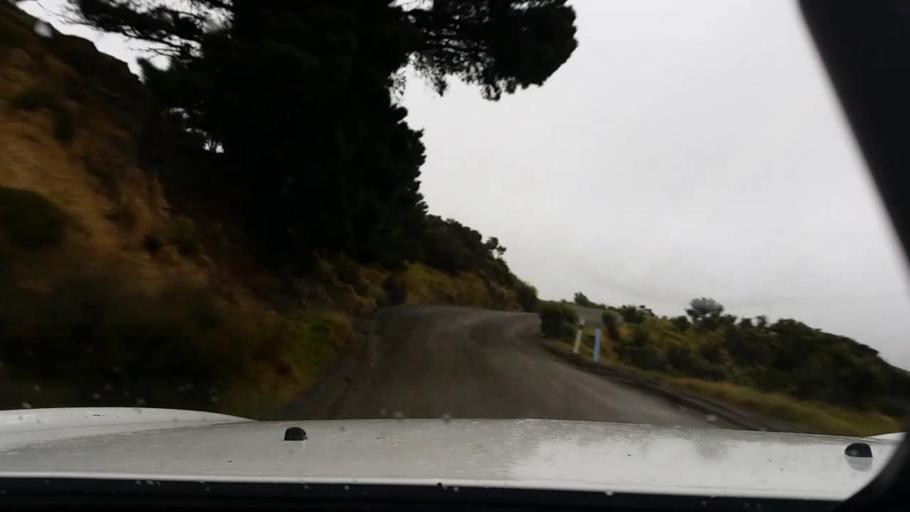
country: NZ
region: Wellington
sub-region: Masterton District
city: Masterton
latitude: -41.2496
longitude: 175.9036
